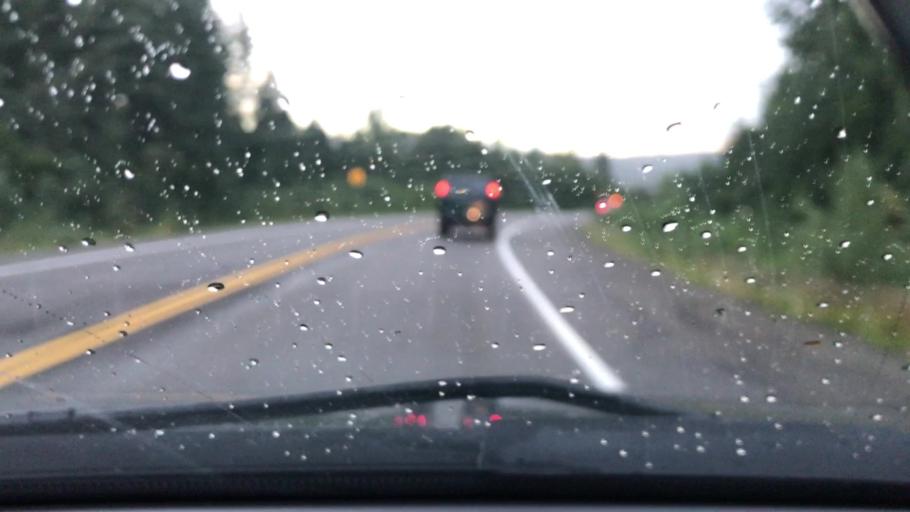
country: US
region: Alaska
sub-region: Matanuska-Susitna Borough
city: Y
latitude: 63.0443
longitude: -149.5814
